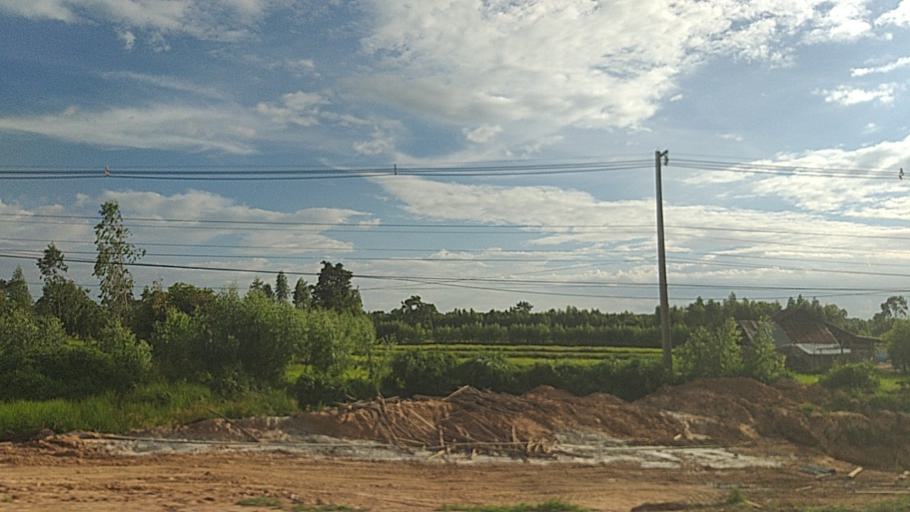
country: TH
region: Surin
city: Kap Choeng
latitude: 14.4859
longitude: 103.5790
